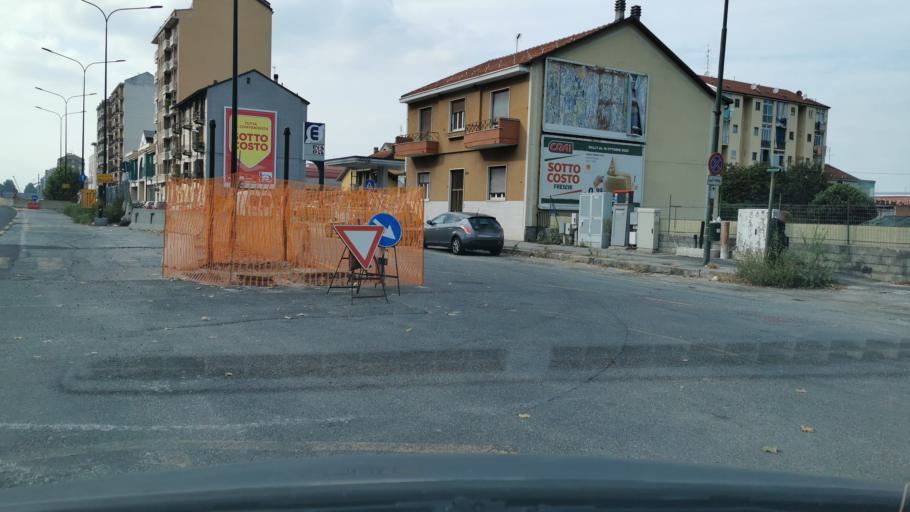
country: IT
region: Piedmont
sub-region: Provincia di Torino
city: Turin
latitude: 45.1048
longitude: 7.6733
